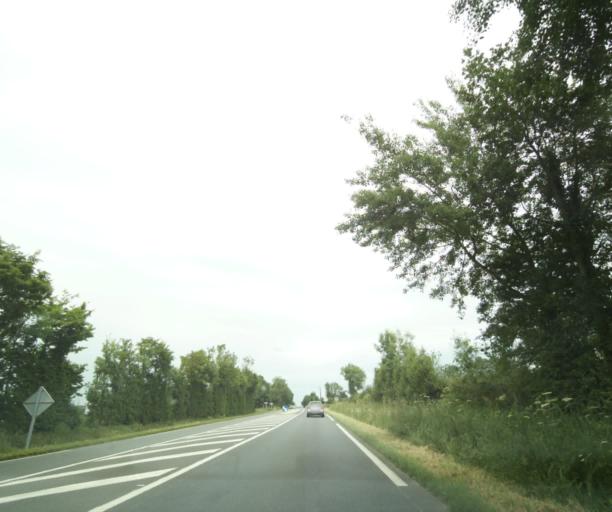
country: FR
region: Poitou-Charentes
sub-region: Departement des Deux-Sevres
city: Champdeniers-Saint-Denis
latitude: 46.4932
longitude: -0.3467
